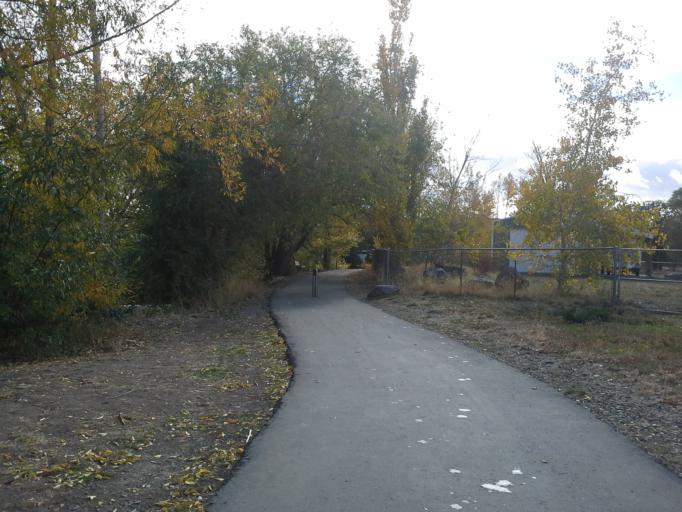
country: US
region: Oregon
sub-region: Baker County
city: Baker City
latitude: 44.7844
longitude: -117.8287
